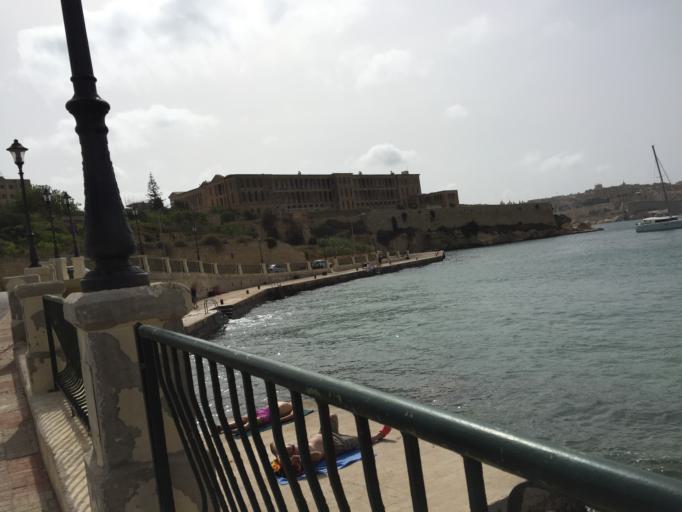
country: MT
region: Il-Kalkara
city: Kalkara
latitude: 35.8931
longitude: 14.5275
